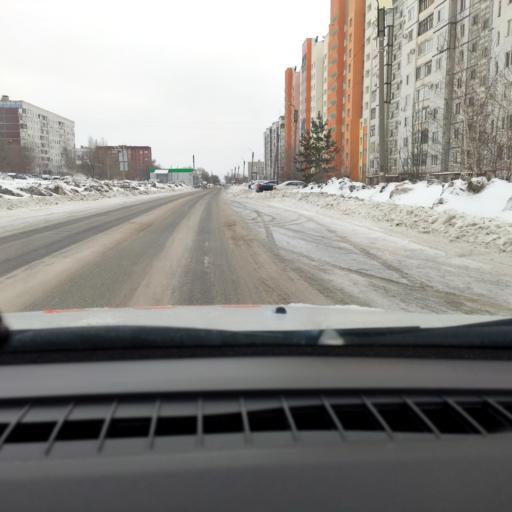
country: RU
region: Samara
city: Novokuybyshevsk
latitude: 53.0900
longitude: 49.9755
